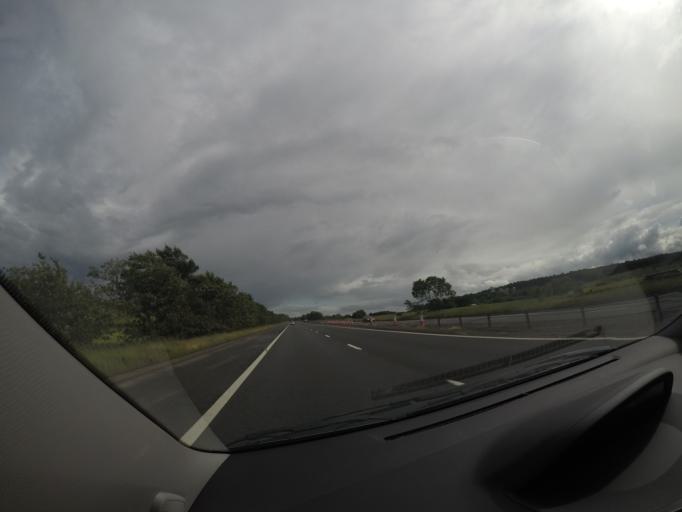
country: GB
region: Scotland
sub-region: Falkirk
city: Dunipace
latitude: 56.0537
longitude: -3.9222
